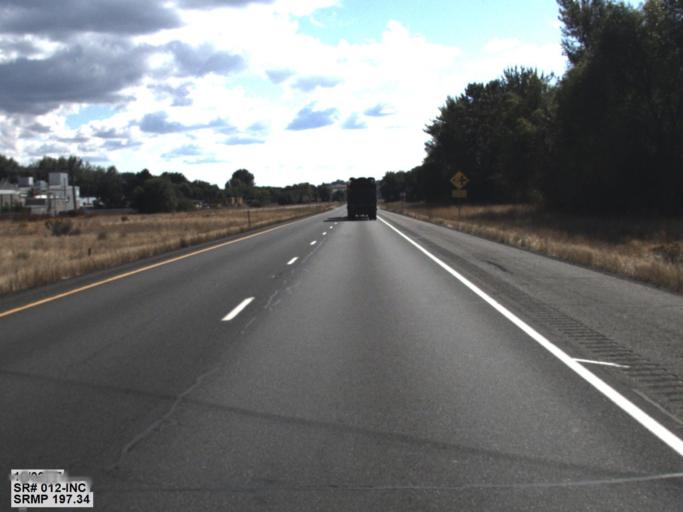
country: US
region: Washington
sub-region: Yakima County
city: Gleed
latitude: 46.6473
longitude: -120.6048
